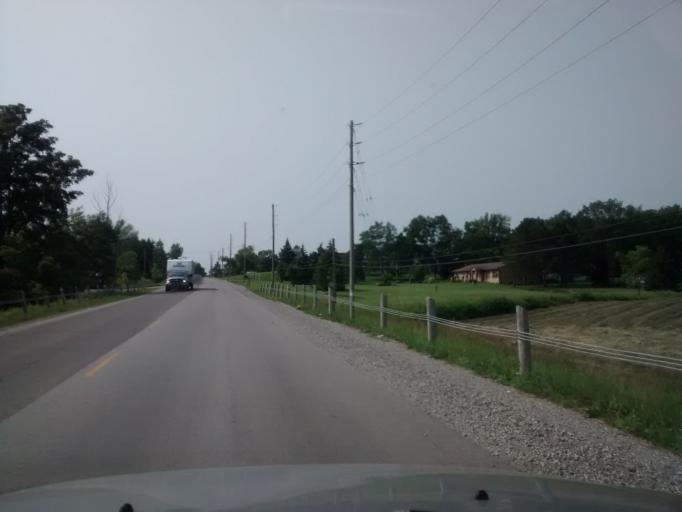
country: CA
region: Ontario
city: Ancaster
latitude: 43.0474
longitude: -79.9085
